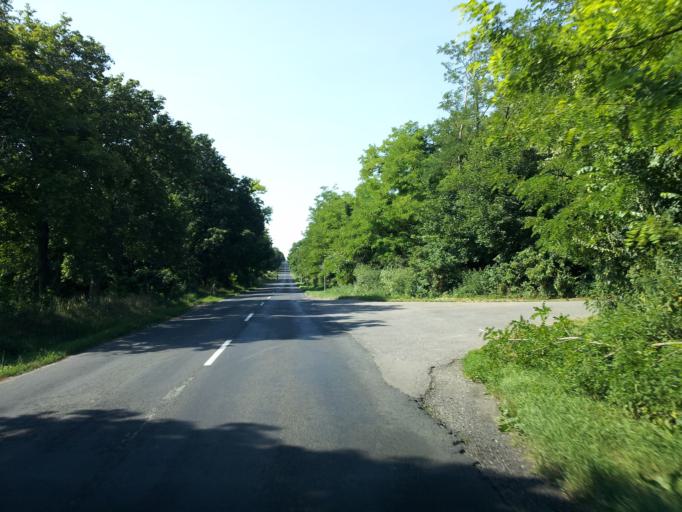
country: HU
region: Fejer
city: Lovasbereny
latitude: 47.3555
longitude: 18.5809
